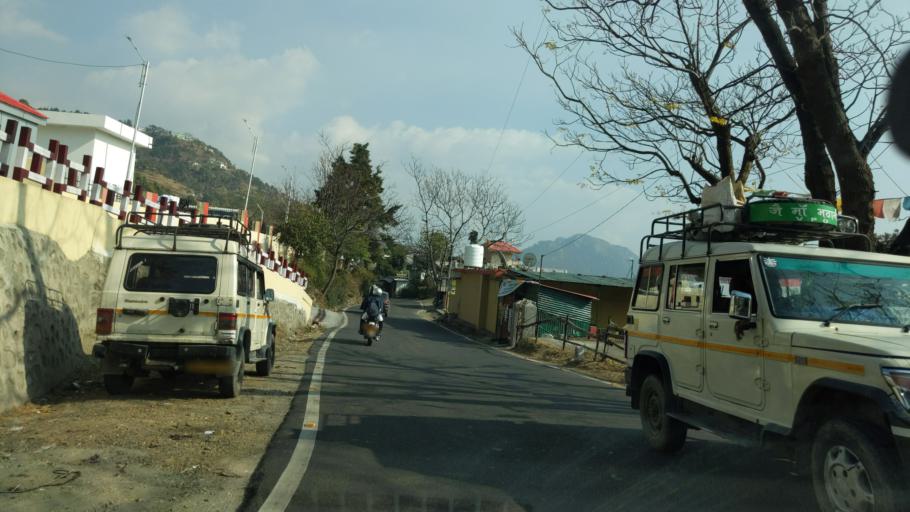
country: IN
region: Uttarakhand
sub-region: Naini Tal
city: Bhowali
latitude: 29.3784
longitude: 79.5262
